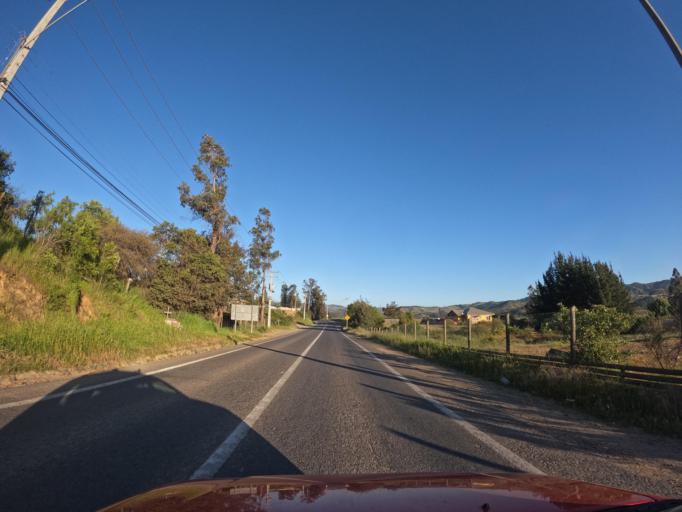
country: CL
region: Maule
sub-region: Provincia de Talca
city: Talca
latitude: -34.9962
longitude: -71.9688
